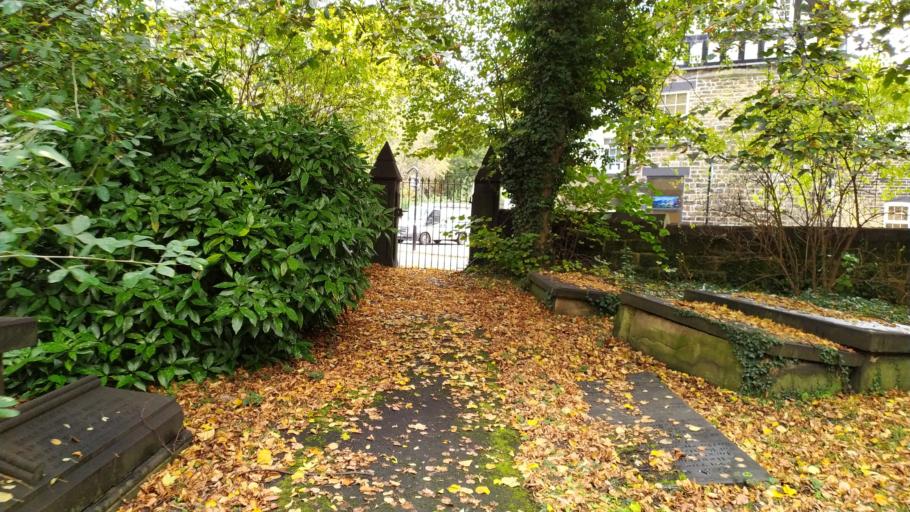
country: GB
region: England
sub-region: City and Borough of Leeds
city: Leeds
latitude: 53.8191
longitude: -1.5757
